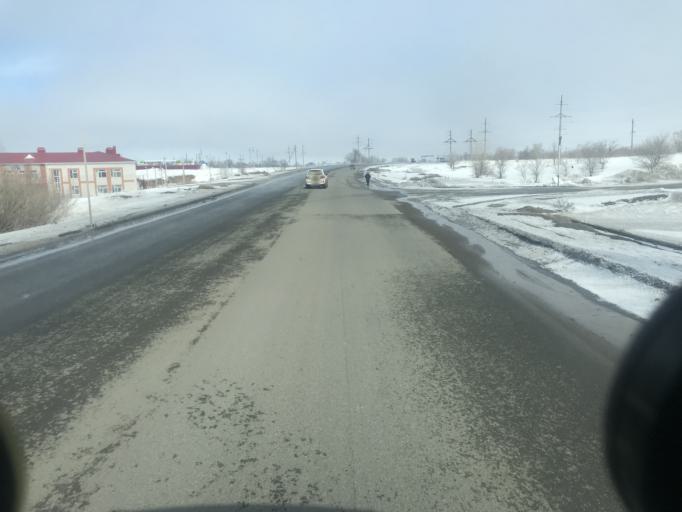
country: KZ
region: Aqtoebe
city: Aqtobe
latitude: 50.2861
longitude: 57.2853
